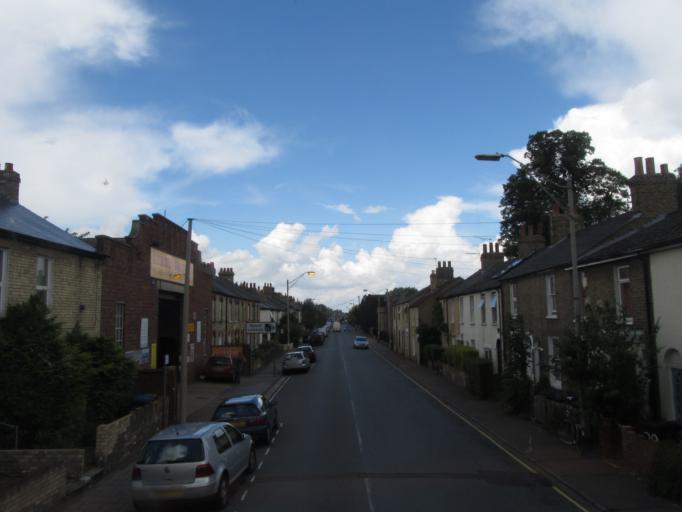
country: GB
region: England
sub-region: Cambridgeshire
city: Cambridge
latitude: 52.2151
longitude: 0.1109
